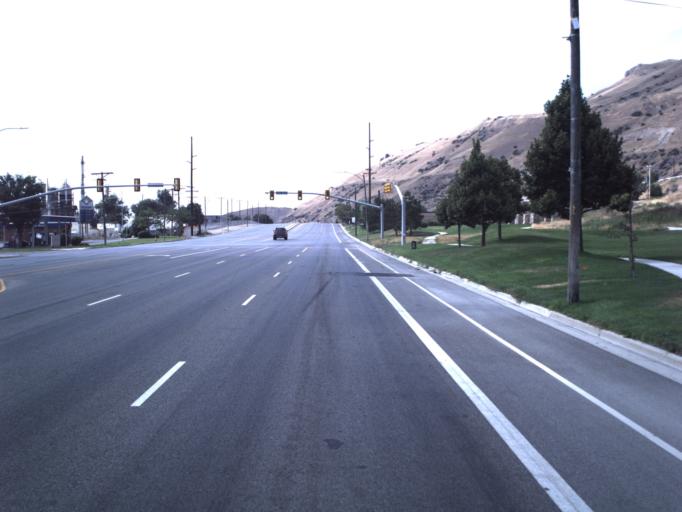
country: US
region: Utah
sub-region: Salt Lake County
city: Salt Lake City
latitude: 40.7893
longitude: -111.9004
